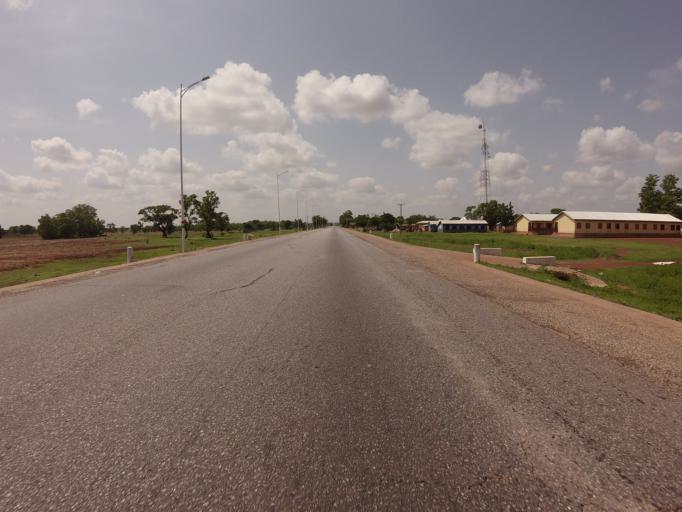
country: GH
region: Northern
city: Savelugu
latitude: 9.5452
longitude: -0.8384
